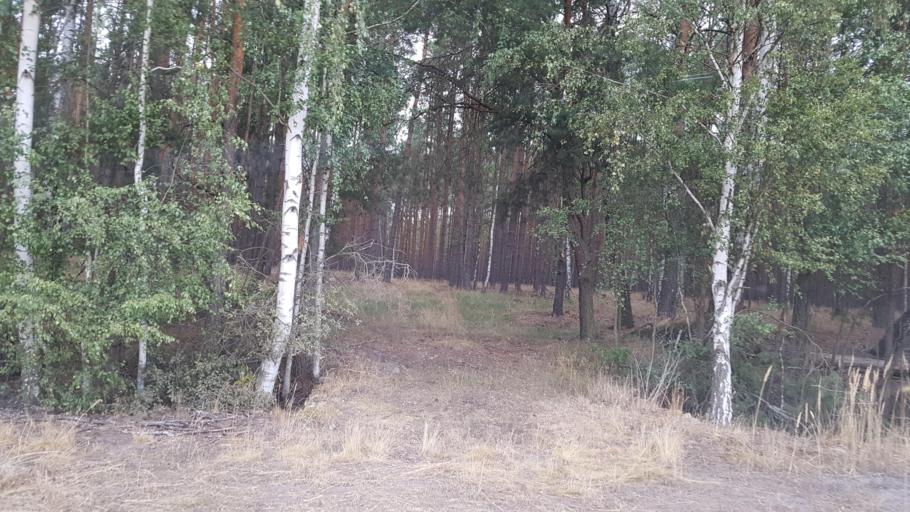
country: DE
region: Brandenburg
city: Sallgast
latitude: 51.6233
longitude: 13.7927
